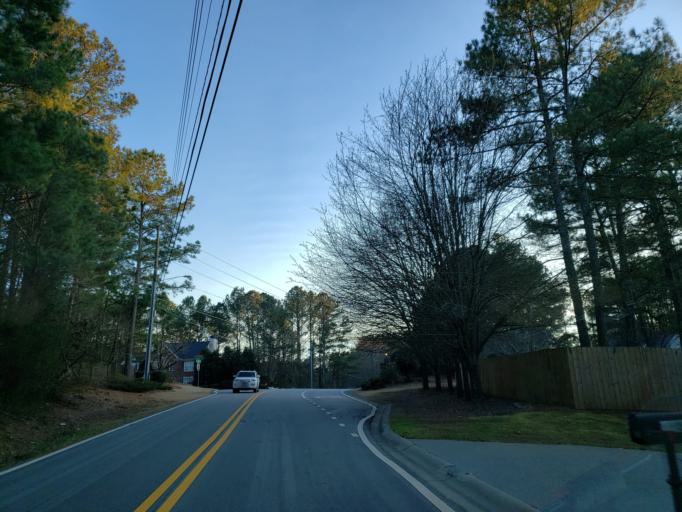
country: US
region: Georgia
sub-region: Cobb County
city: Acworth
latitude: 34.0091
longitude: -84.7465
